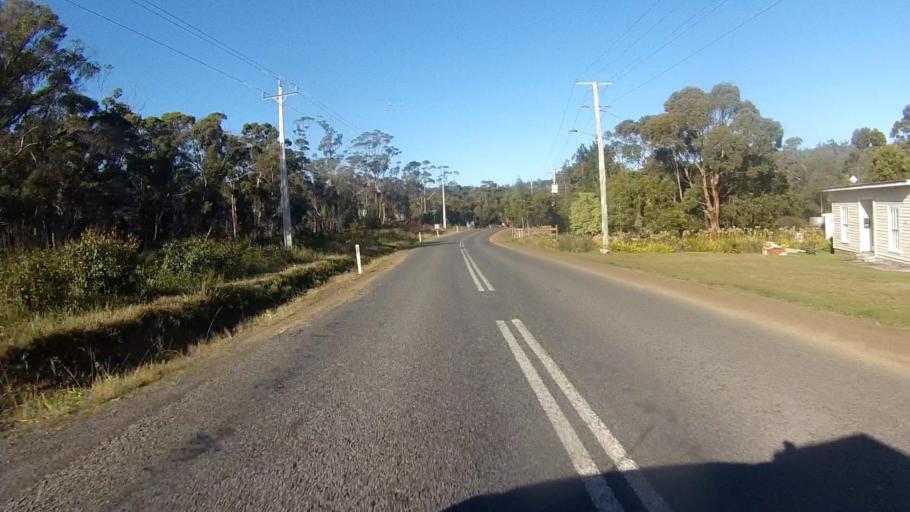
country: AU
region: Tasmania
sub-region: Sorell
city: Sorell
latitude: -42.9422
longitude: 147.8639
